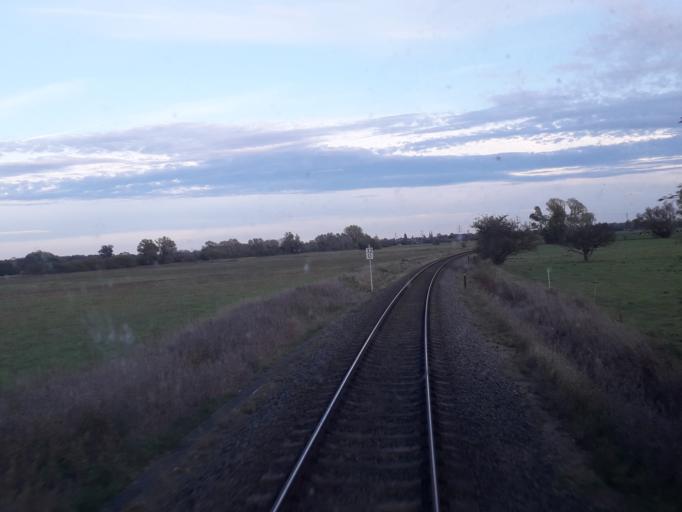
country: DE
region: Brandenburg
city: Dabergotz
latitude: 52.9334
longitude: 12.7577
